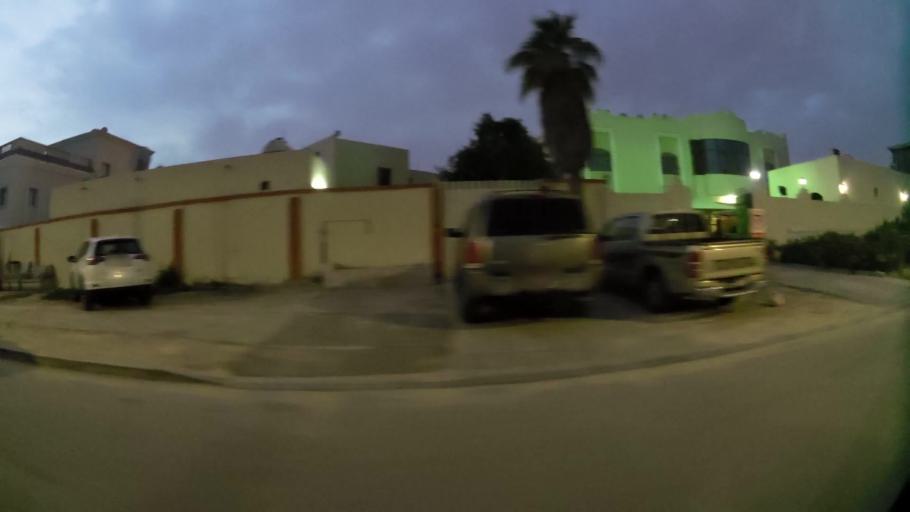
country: QA
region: Baladiyat ad Dawhah
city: Doha
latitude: 25.3441
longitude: 51.5067
